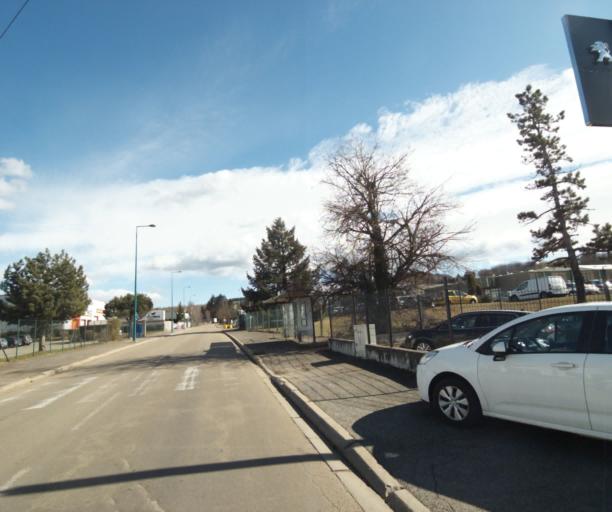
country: FR
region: Rhone-Alpes
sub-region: Departement de la Loire
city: La Talaudiere
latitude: 45.4752
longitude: 4.4274
